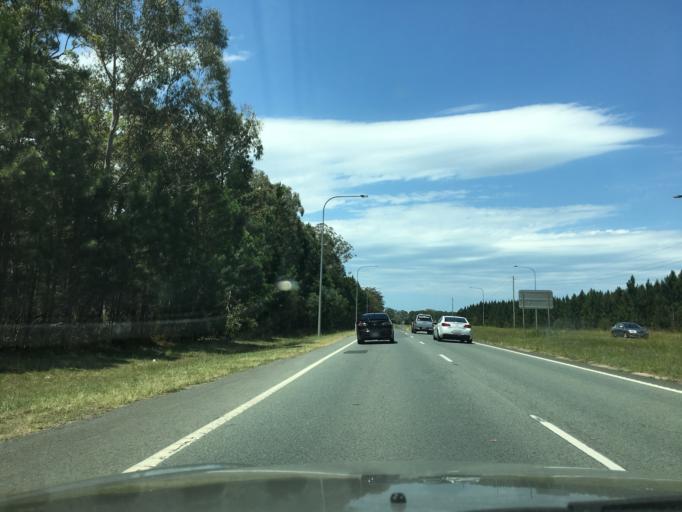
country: AU
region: Queensland
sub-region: Moreton Bay
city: Caboolture
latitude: -27.0760
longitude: 153.0426
